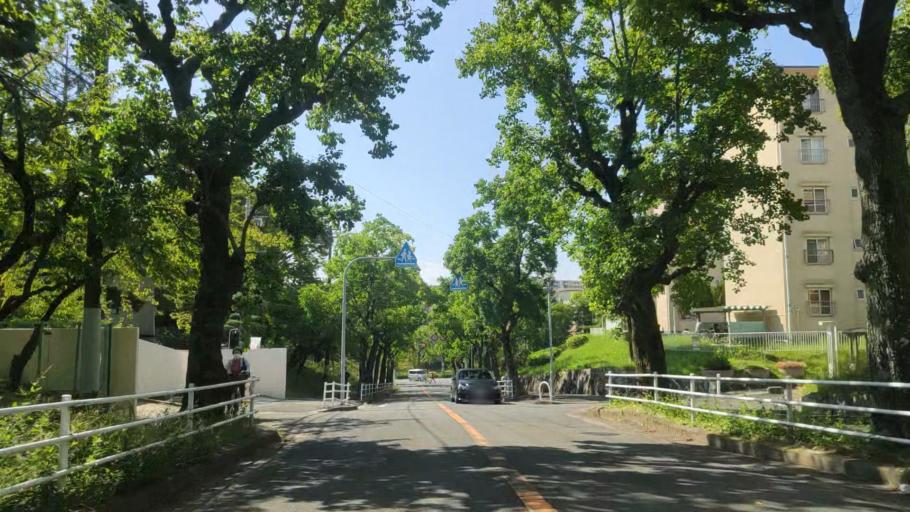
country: JP
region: Osaka
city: Mino
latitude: 34.8227
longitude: 135.5073
